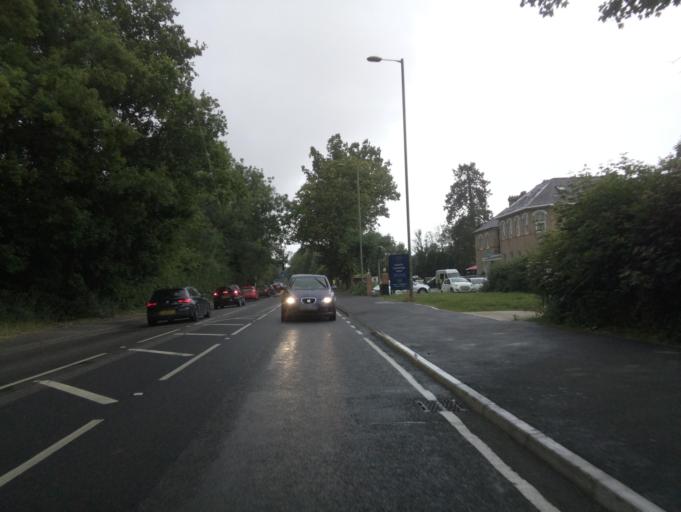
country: GB
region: England
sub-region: Surrey
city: Horley
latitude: 51.1878
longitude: -0.1637
